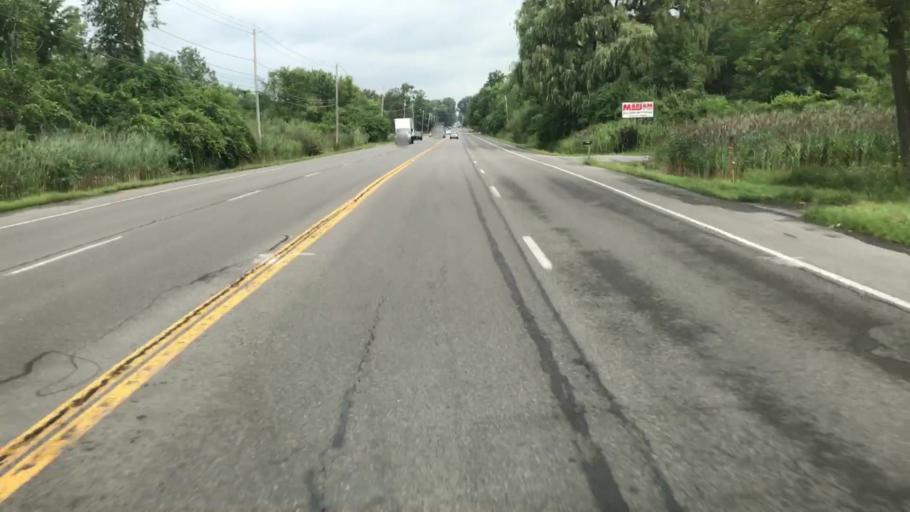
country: US
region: New York
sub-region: Onondaga County
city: Liverpool
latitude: 43.1437
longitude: -76.2070
